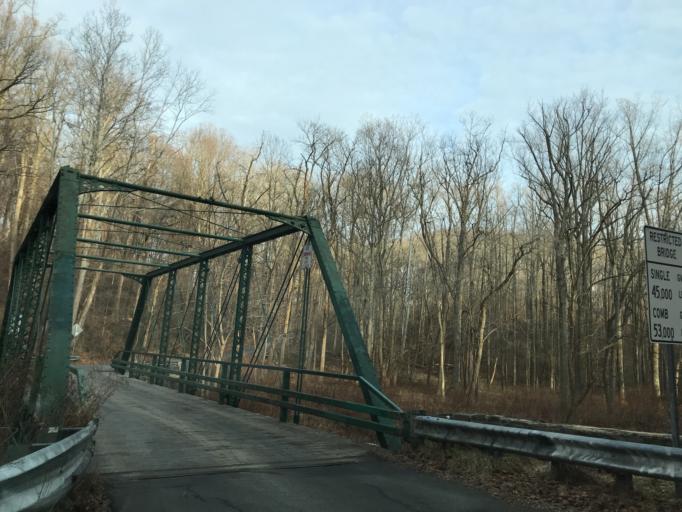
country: US
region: Maryland
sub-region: Harford County
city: Joppatowne
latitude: 39.4472
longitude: -76.3814
